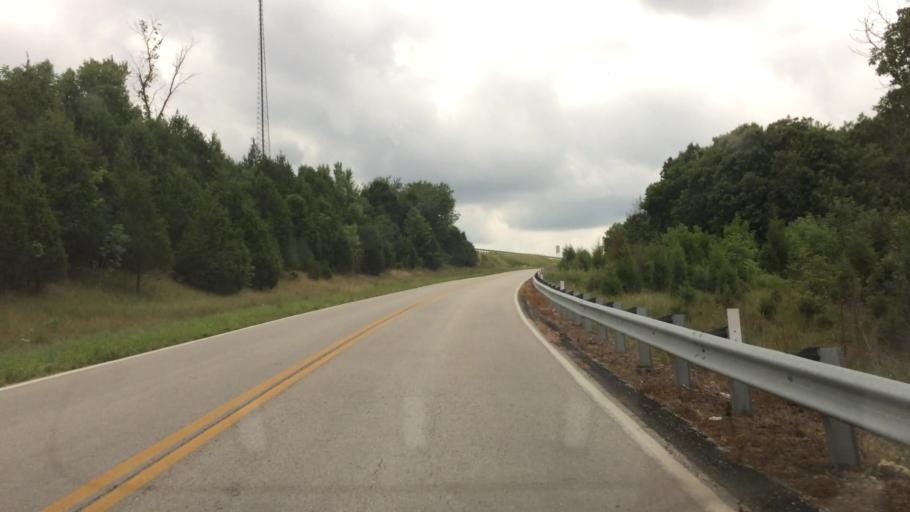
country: US
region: Missouri
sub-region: Webster County
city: Marshfield
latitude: 37.3023
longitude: -93.0083
